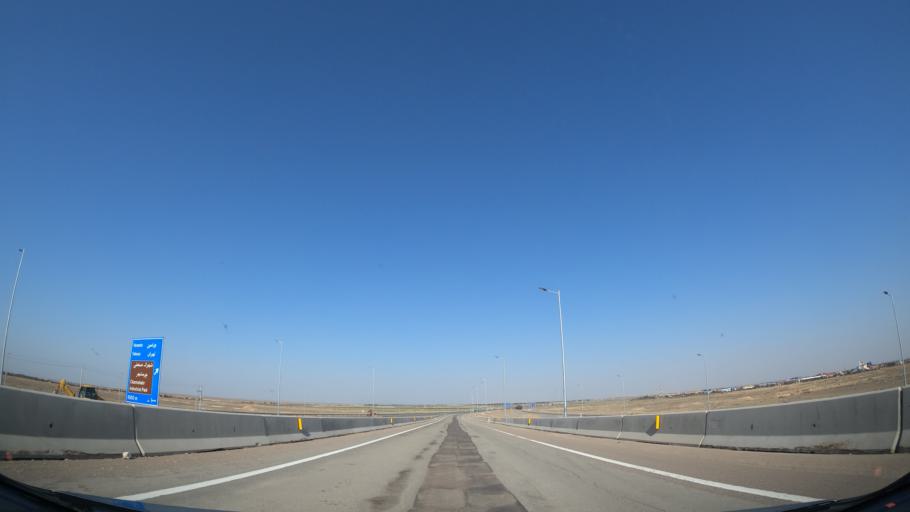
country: IR
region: Tehran
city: Eqbaliyeh
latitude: 35.1357
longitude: 51.5200
